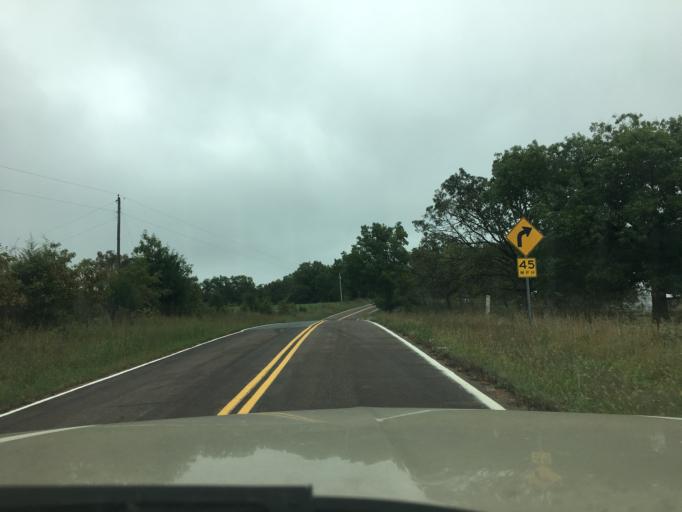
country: US
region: Missouri
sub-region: Crawford County
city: Cuba
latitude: 38.1927
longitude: -91.4677
